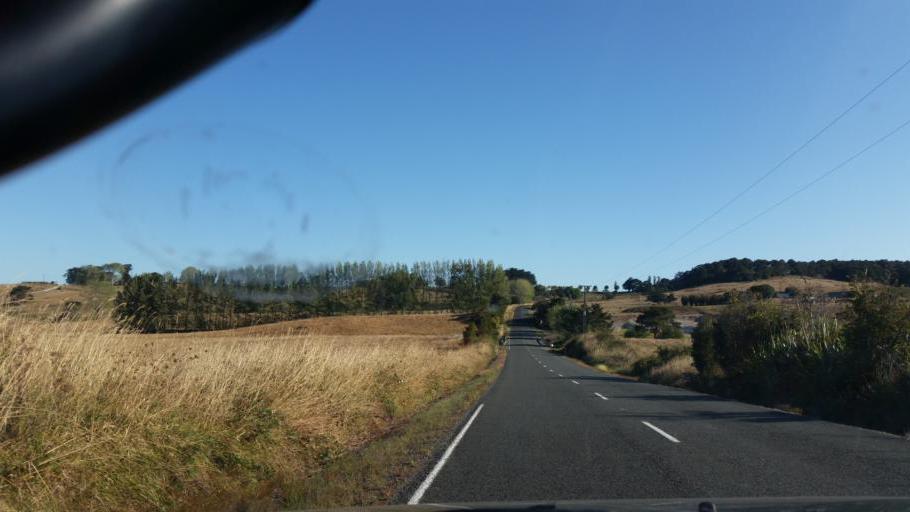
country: NZ
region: Northland
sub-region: Kaipara District
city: Dargaville
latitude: -36.0820
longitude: 174.1713
